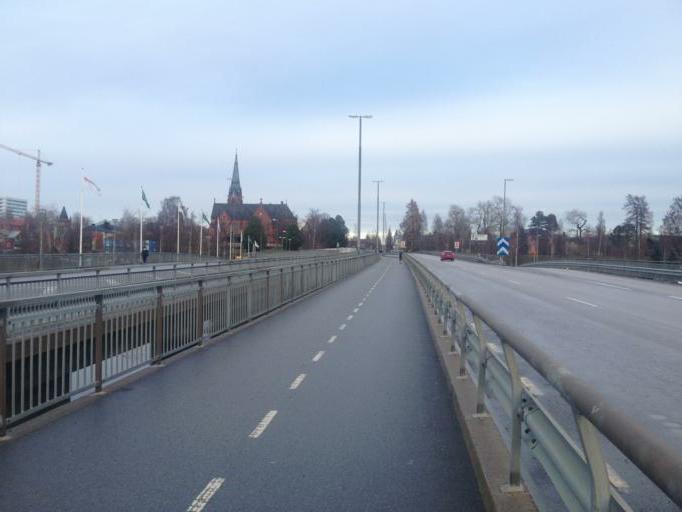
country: SE
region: Vaesterbotten
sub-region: Umea Kommun
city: Umea
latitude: 63.8208
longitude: 20.2670
